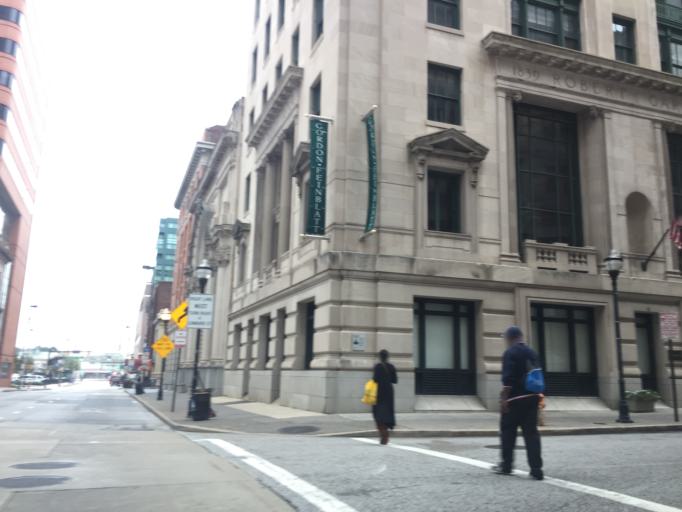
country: US
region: Maryland
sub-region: City of Baltimore
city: Baltimore
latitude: 39.2890
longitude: -76.6110
